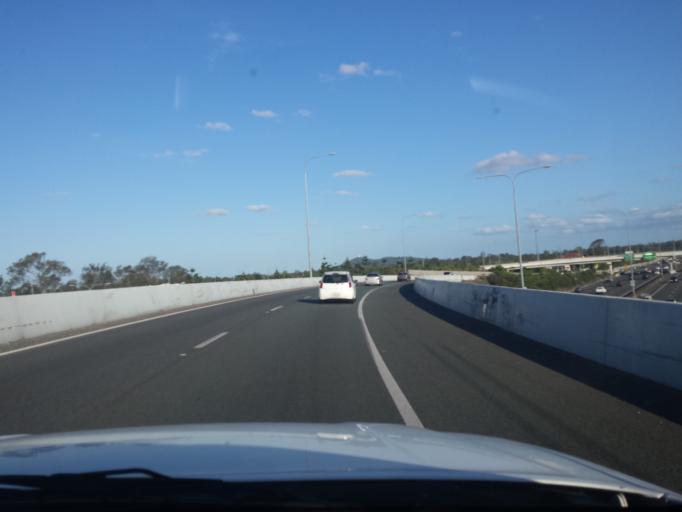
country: AU
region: Queensland
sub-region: Logan
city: Beenleigh
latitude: -27.6860
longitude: 153.1894
